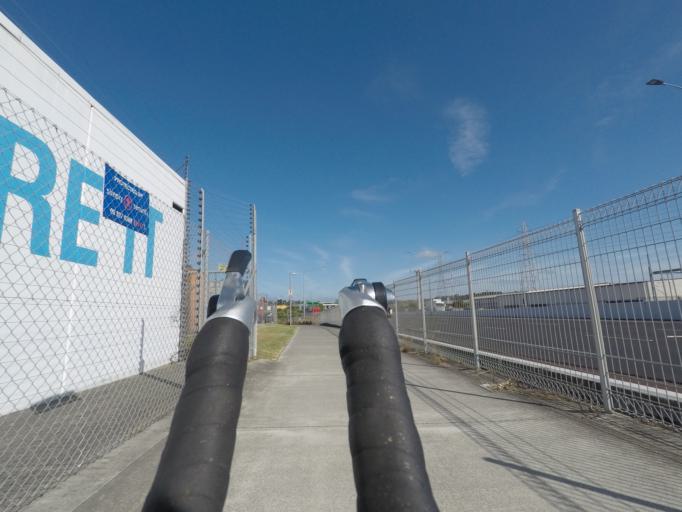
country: NZ
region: Auckland
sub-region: Auckland
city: Rosebank
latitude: -36.8518
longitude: 174.6373
